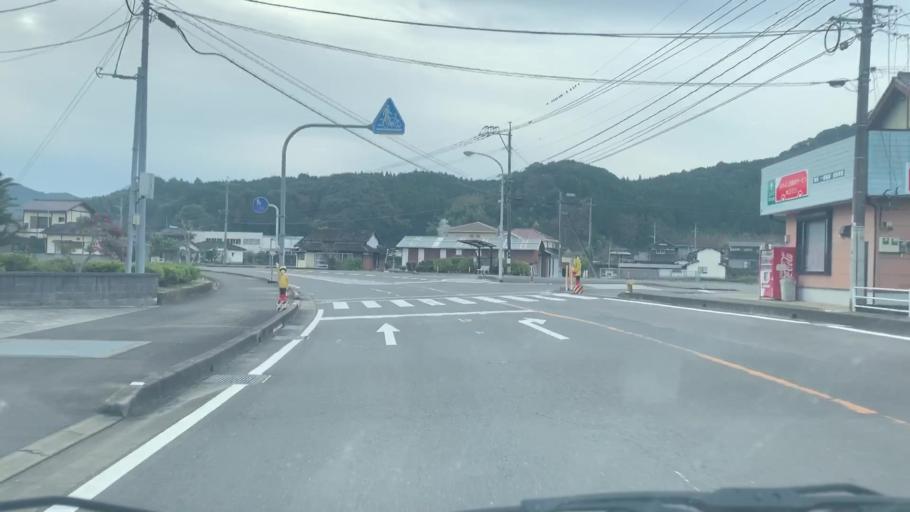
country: JP
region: Saga Prefecture
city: Takeocho-takeo
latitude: 33.1692
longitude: 130.0505
